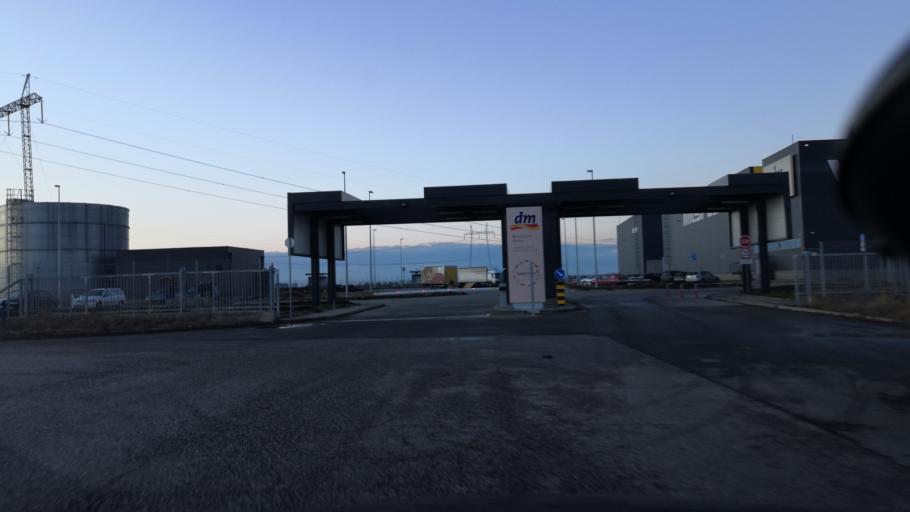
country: RS
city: Simanovci
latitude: 44.8912
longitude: 20.1086
